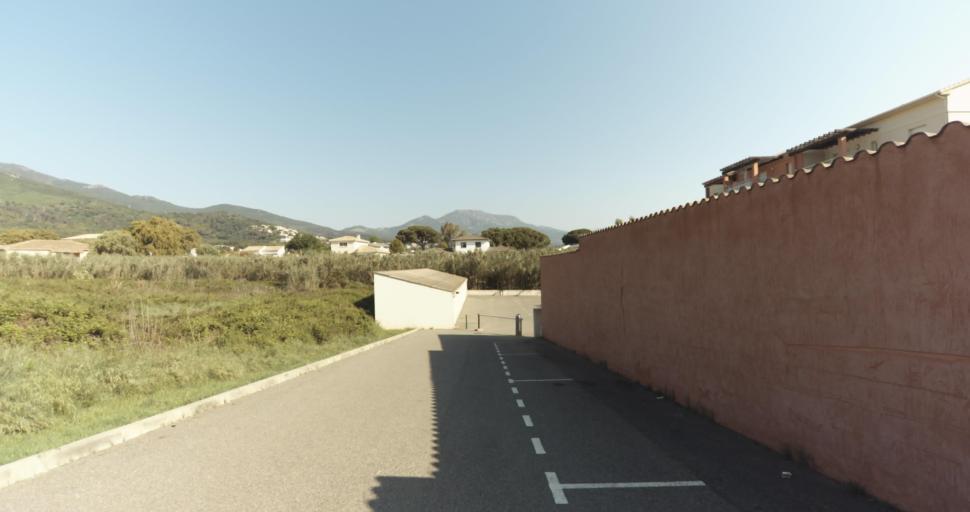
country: FR
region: Corsica
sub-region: Departement de la Haute-Corse
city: Biguglia
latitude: 42.6299
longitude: 9.4342
